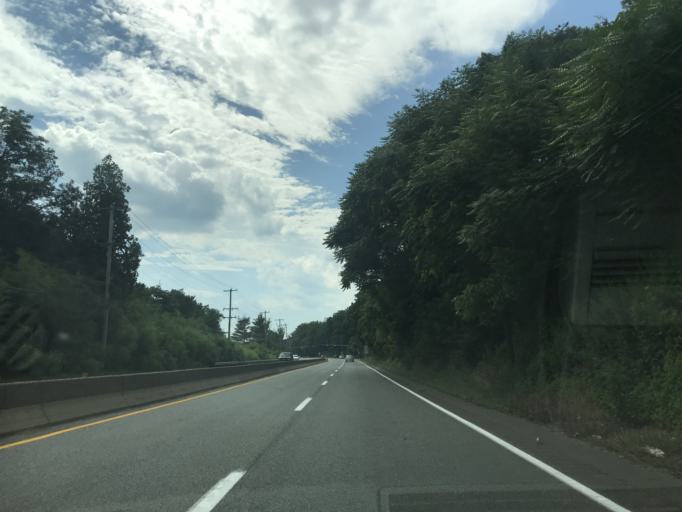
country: US
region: Pennsylvania
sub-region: Chester County
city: West Chester
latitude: 39.8736
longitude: -75.5749
